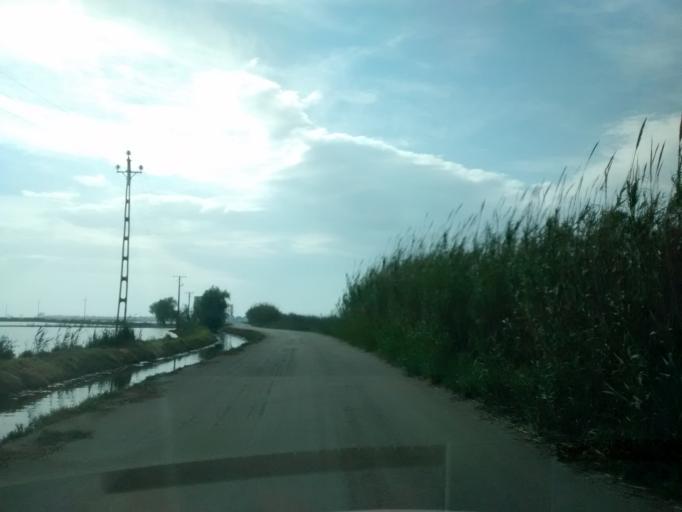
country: ES
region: Catalonia
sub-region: Provincia de Tarragona
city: Deltebre
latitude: 40.6985
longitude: 0.8319
